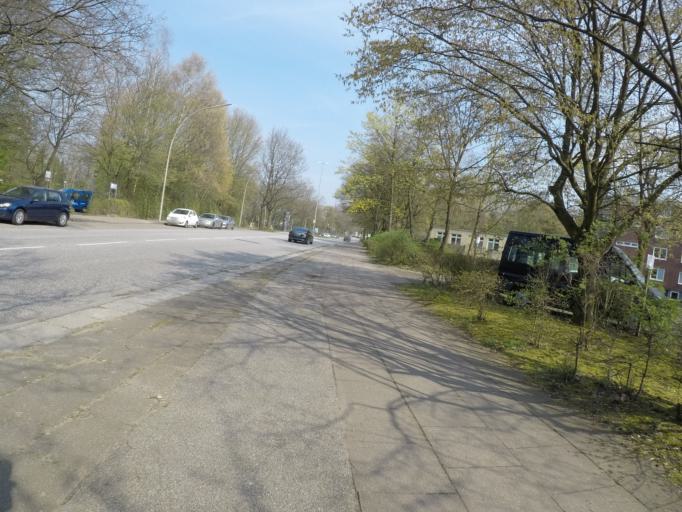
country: DE
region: Hamburg
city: Hummelsbuettel
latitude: 53.6454
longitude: 10.0529
